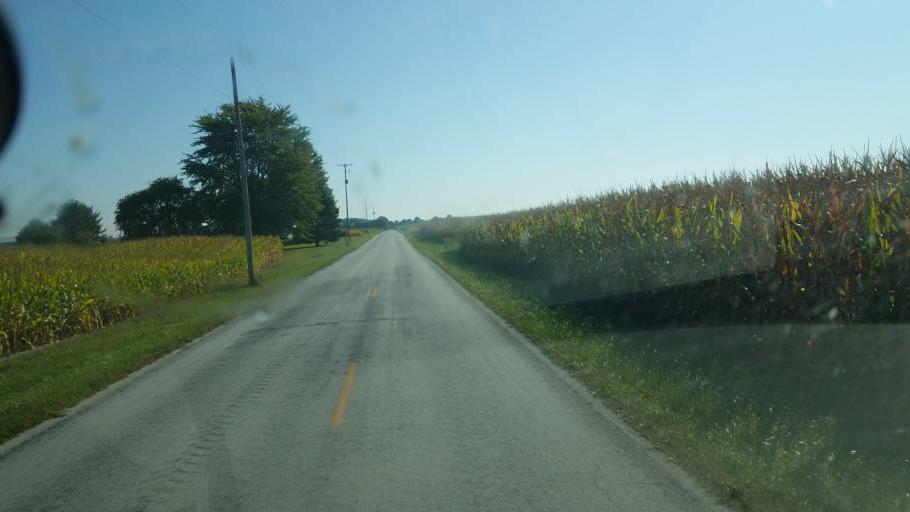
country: US
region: Ohio
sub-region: Hardin County
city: Kenton
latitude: 40.6125
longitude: -83.5784
